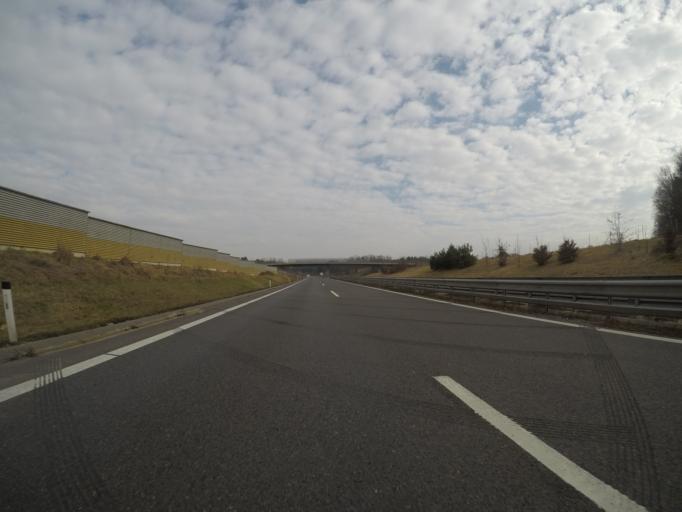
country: SI
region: Cerkvenjak
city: Cerkvenjak
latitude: 46.5827
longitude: 15.9802
